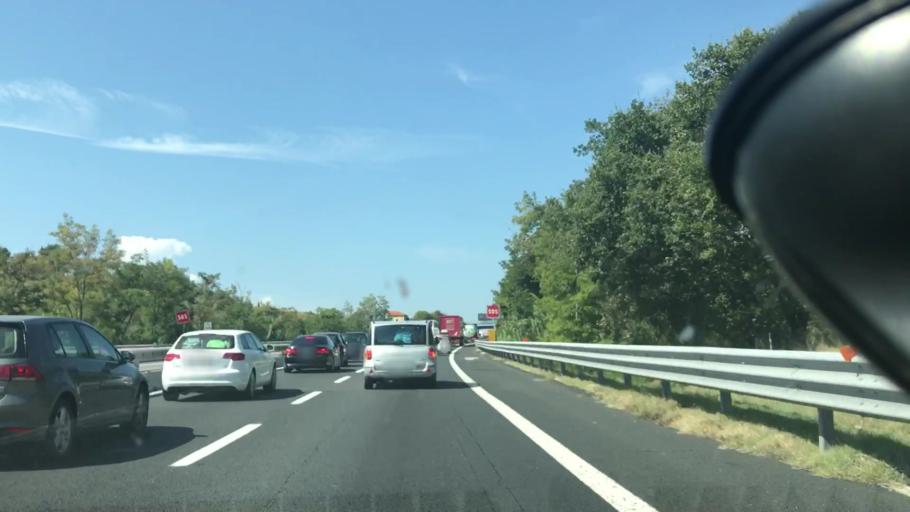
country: IT
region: Abruzzo
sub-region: Provincia di Chieti
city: Torino di Sangro
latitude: 42.2046
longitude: 14.5328
